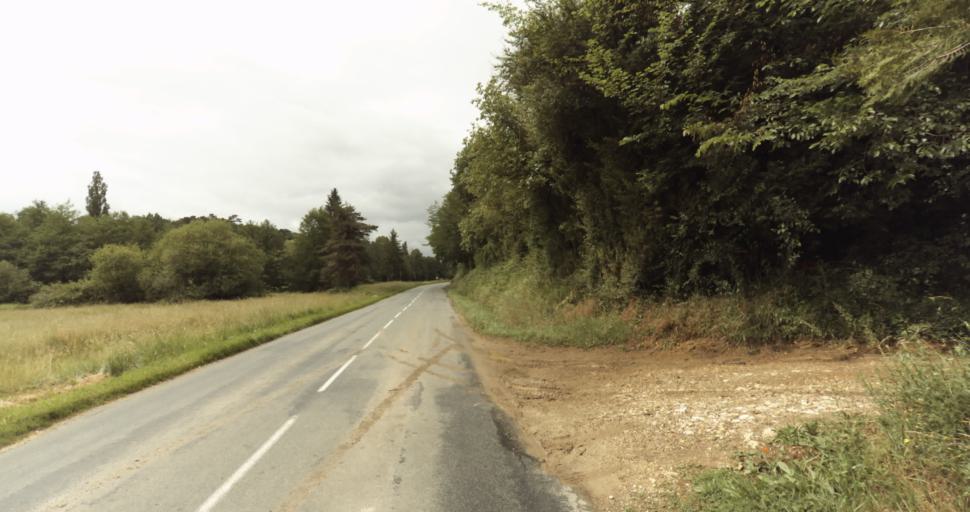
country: FR
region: Aquitaine
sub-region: Departement du Lot-et-Garonne
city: Villereal
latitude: 44.6719
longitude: 0.8867
